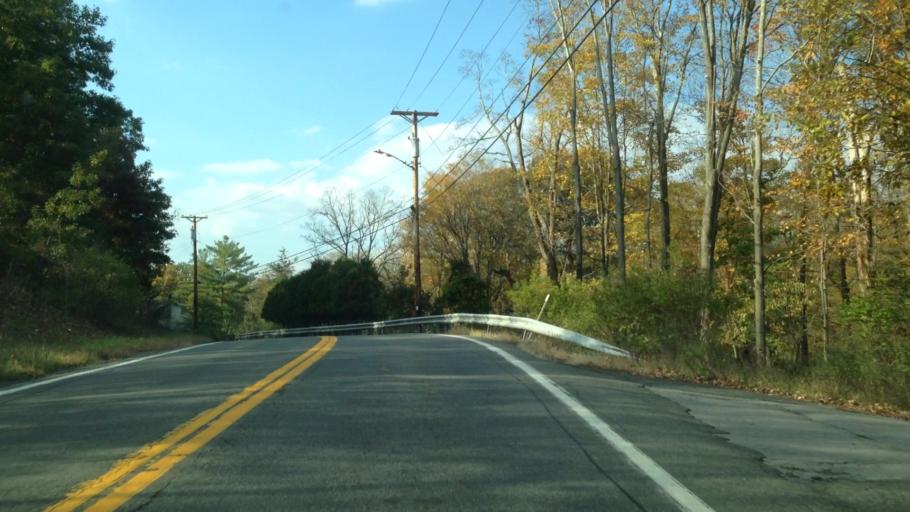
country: US
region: New York
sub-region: Ulster County
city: Tillson
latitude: 41.8370
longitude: -74.0429
